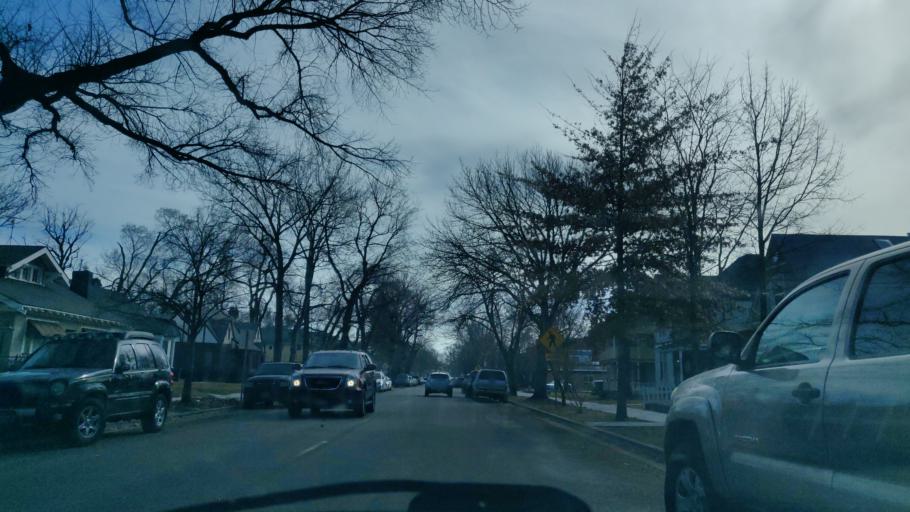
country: US
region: Idaho
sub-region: Ada County
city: Boise
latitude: 43.6248
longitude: -116.1976
